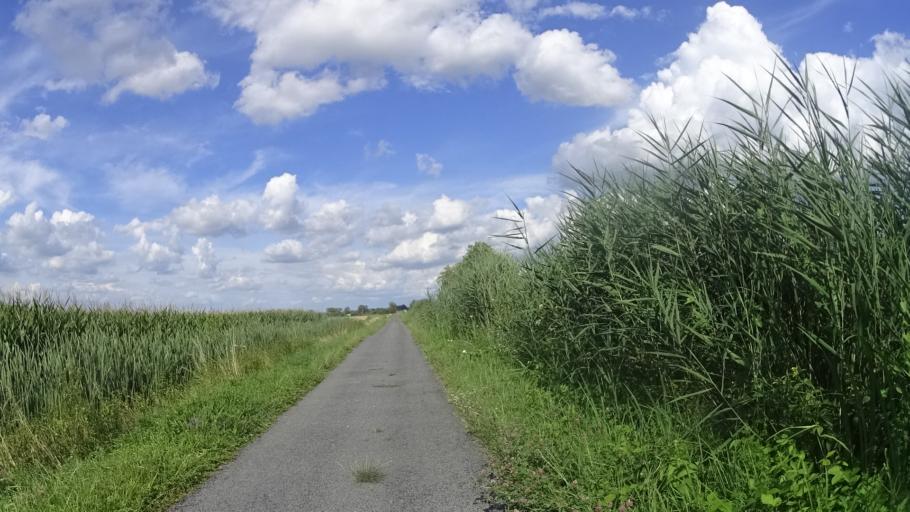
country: FR
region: Champagne-Ardenne
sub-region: Departement de la Marne
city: Sermaize-les-Bains
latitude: 48.7852
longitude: 4.8768
